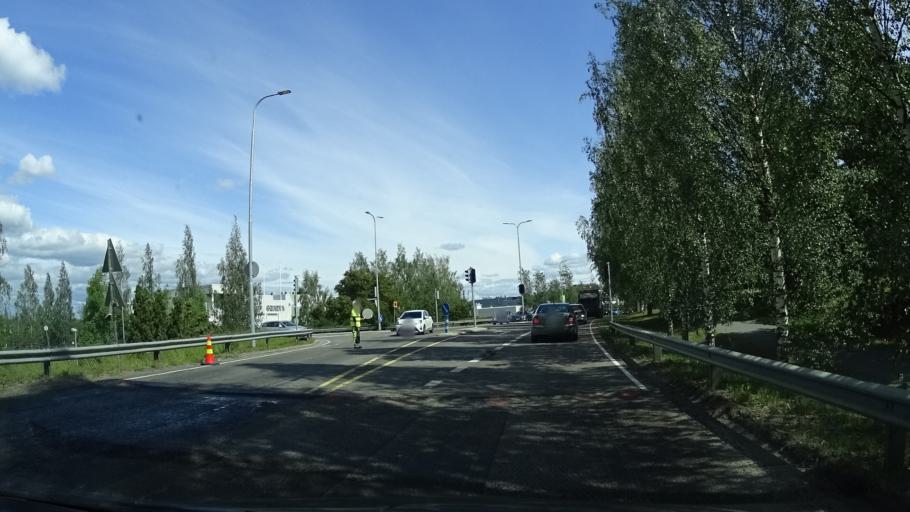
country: FI
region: Central Finland
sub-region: Jyvaeskylae
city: Jyvaeskylae
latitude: 62.2450
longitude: 25.7199
